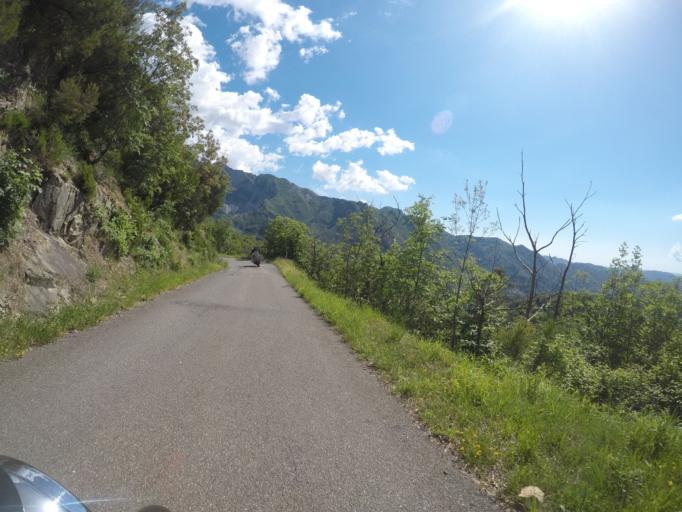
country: IT
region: Tuscany
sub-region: Provincia di Massa-Carrara
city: Casola in Lunigiana
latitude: 44.1796
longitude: 10.1659
